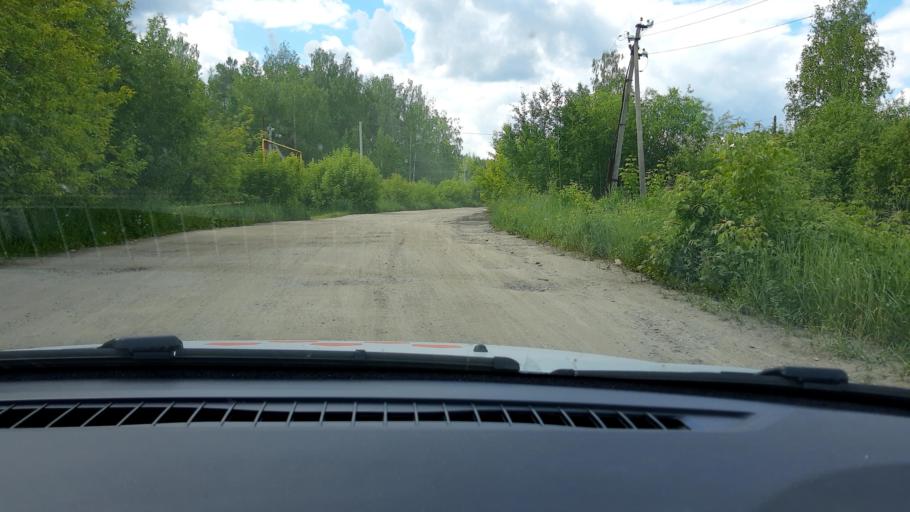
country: RU
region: Nizjnij Novgorod
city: Kstovo
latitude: 56.1700
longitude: 44.1635
